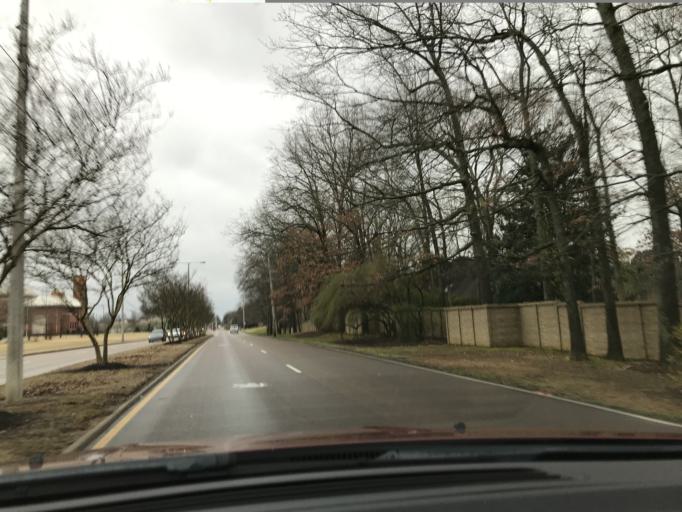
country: US
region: Tennessee
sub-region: Shelby County
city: Collierville
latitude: 35.0646
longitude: -89.6859
